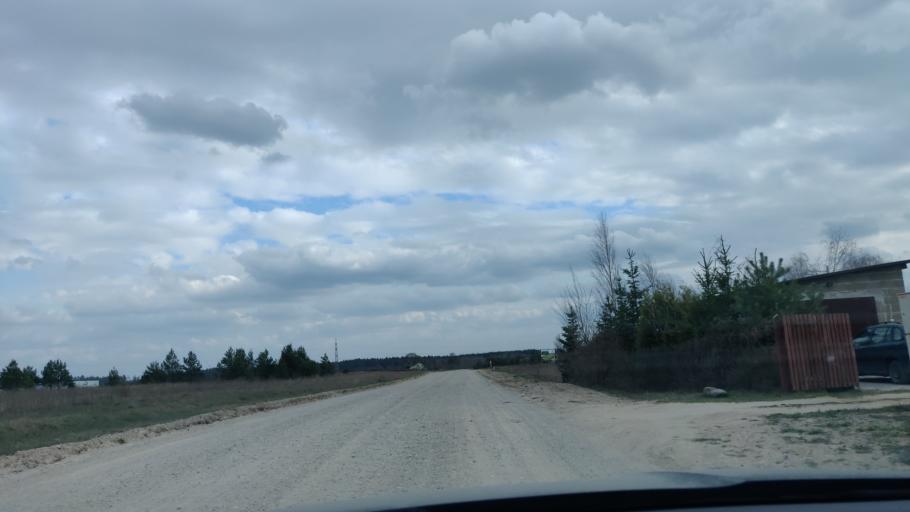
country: LT
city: Lentvaris
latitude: 54.6147
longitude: 25.0687
